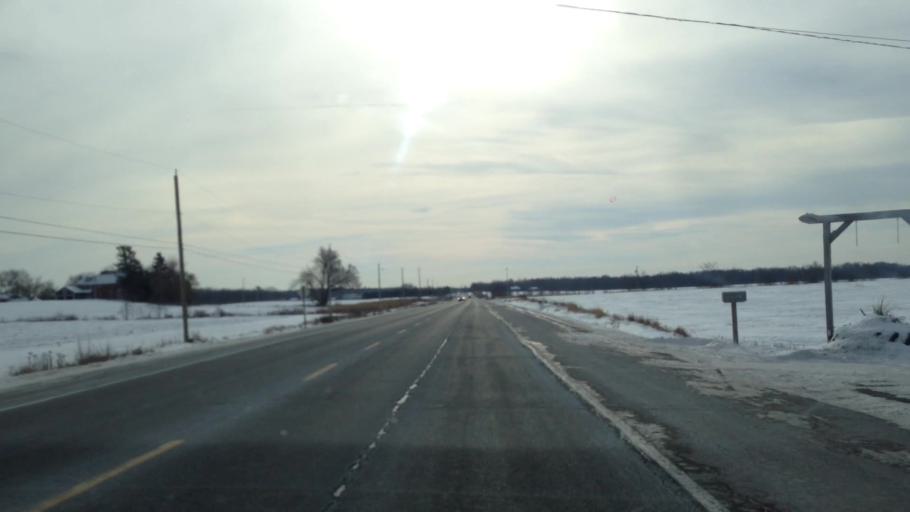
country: CA
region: Ontario
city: Clarence-Rockland
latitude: 45.4051
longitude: -75.3990
